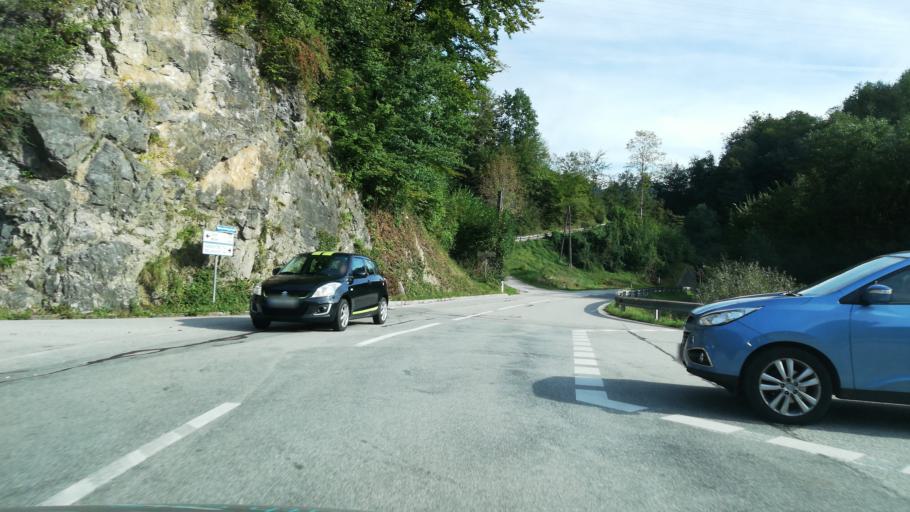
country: AT
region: Upper Austria
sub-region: Politischer Bezirk Steyr-Land
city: Maria Neustift
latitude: 47.8917
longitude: 14.5401
